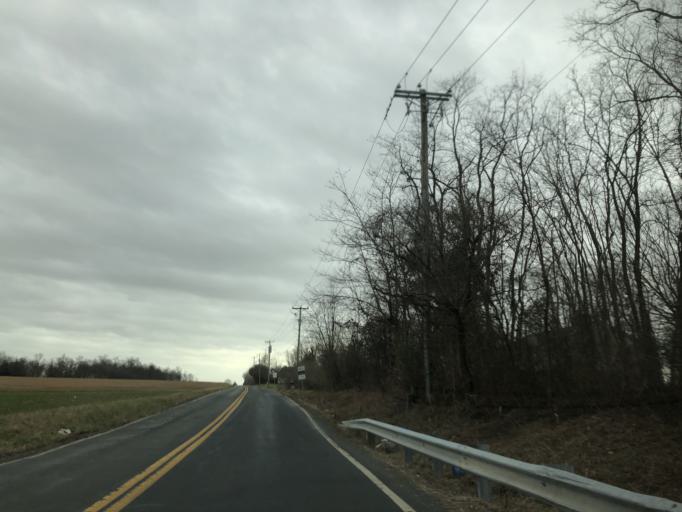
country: US
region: Pennsylvania
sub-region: Chester County
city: Oxford
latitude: 39.6999
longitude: -75.9528
